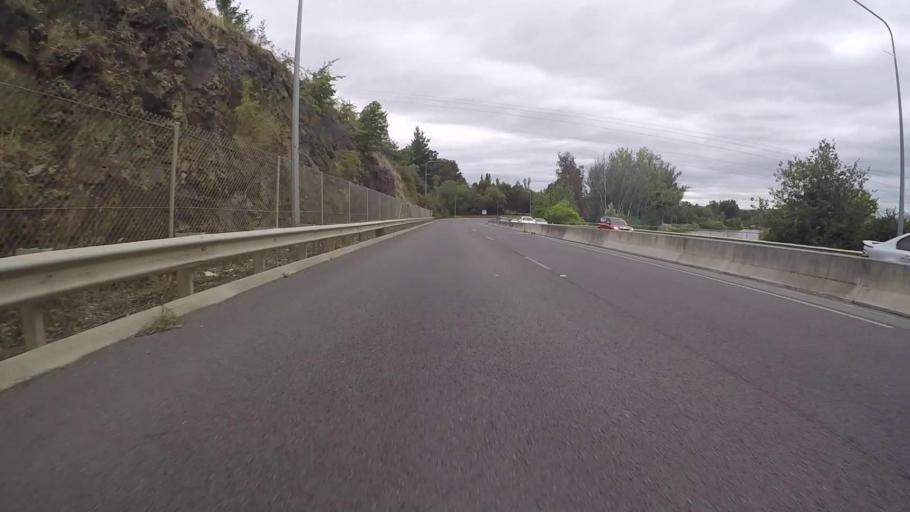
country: AU
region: Australian Capital Territory
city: Forrest
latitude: -35.3016
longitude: 149.1575
